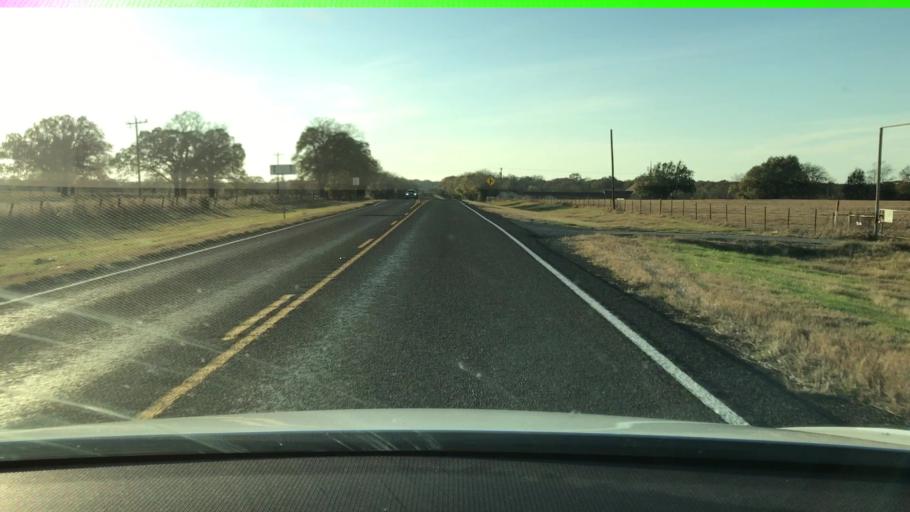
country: US
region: Texas
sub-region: Kaufman County
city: Kemp
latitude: 32.5703
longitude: -96.1259
